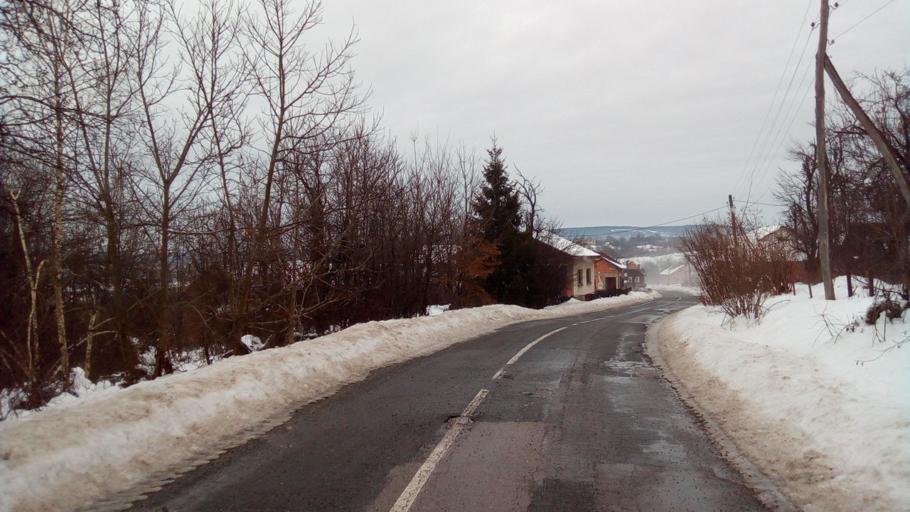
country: HR
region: Sisacko-Moslavacka
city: Petrinja
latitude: 45.3465
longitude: 16.2486
